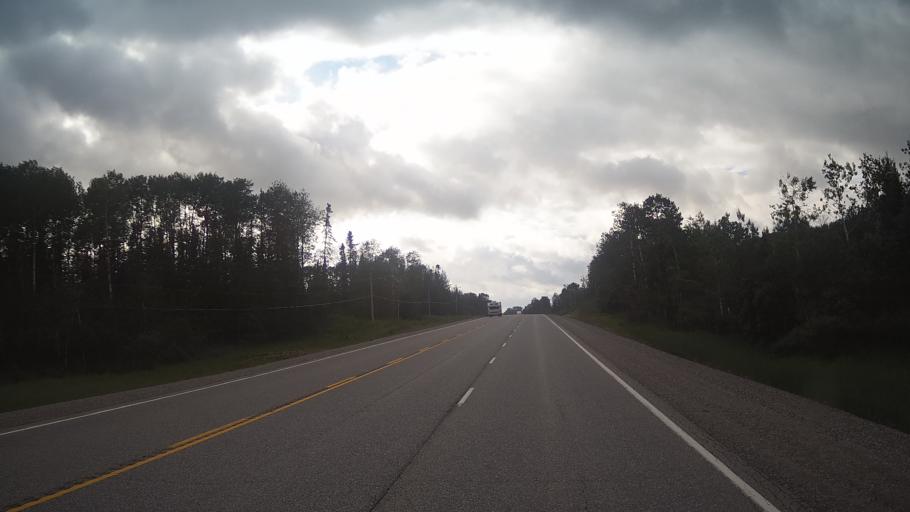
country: CA
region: Ontario
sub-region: Rainy River District
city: Atikokan
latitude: 49.0021
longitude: -90.4064
